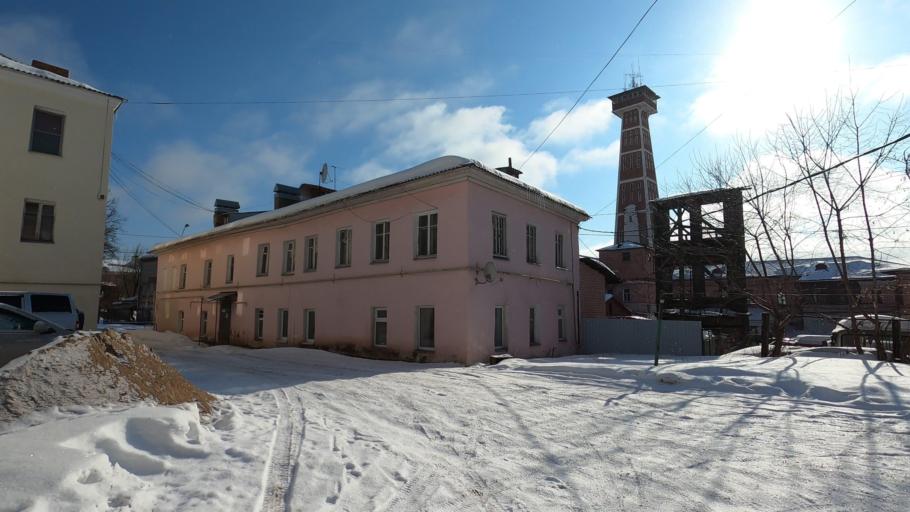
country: RU
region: Jaroslavl
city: Rybinsk
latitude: 58.0471
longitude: 38.8520
